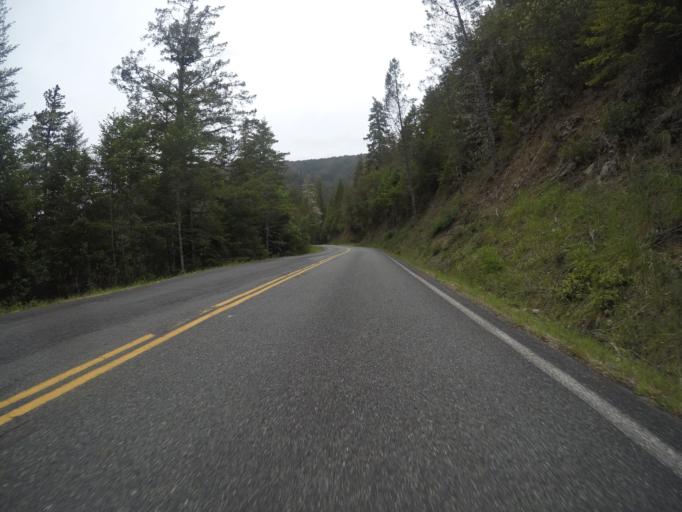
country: US
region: California
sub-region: Del Norte County
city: Bertsch-Oceanview
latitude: 41.7642
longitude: -124.0051
